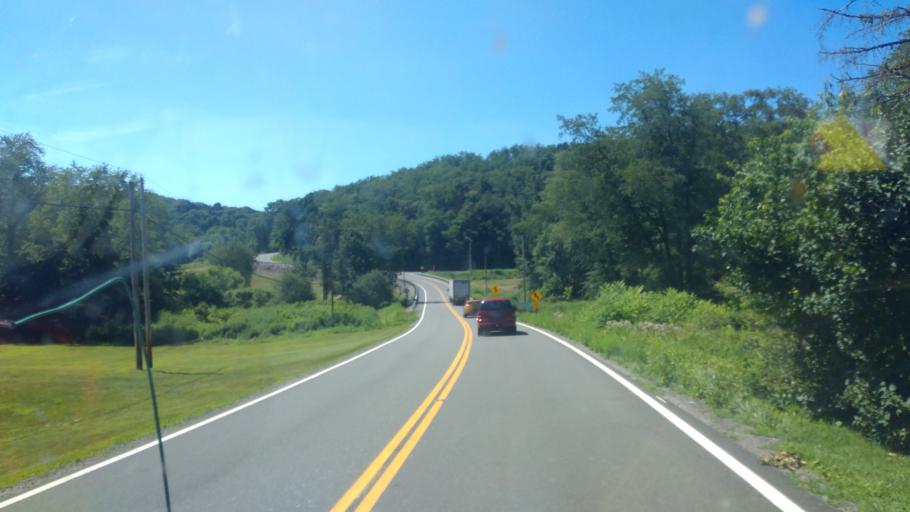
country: US
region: Ohio
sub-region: Carroll County
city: Carrollton
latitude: 40.5013
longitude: -80.9789
